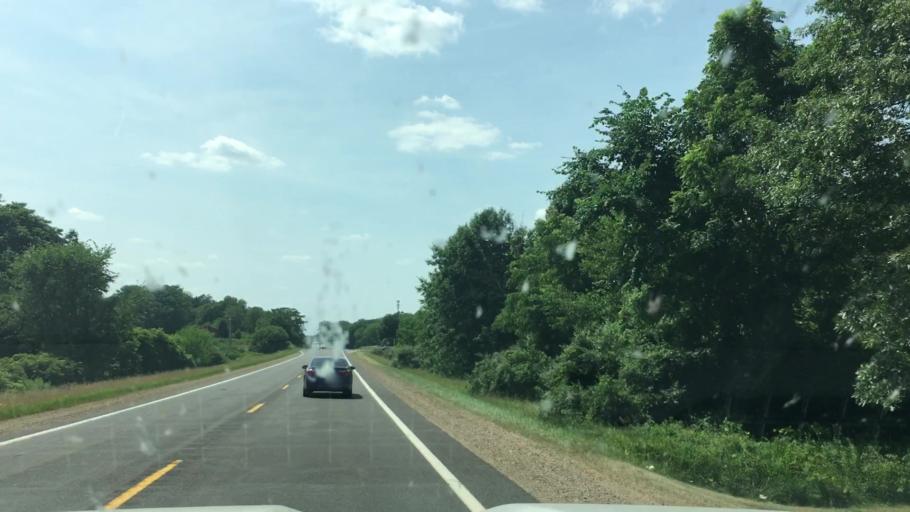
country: US
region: Michigan
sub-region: Allegan County
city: Plainwell
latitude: 42.4332
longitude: -85.5571
